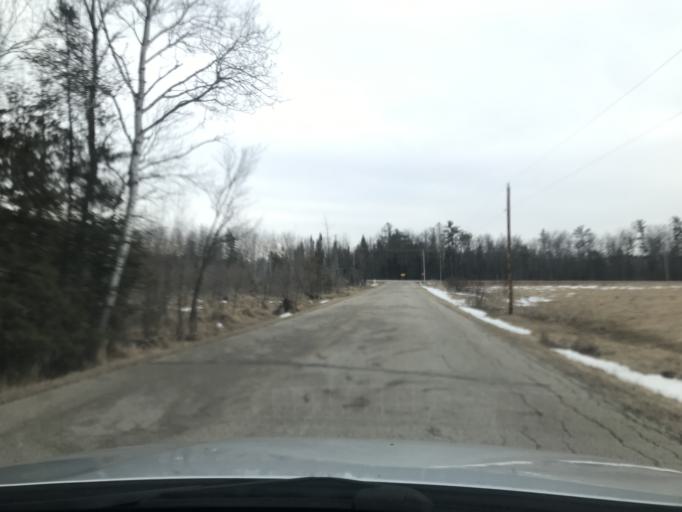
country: US
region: Wisconsin
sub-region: Marinette County
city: Peshtigo
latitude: 45.1105
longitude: -88.0082
